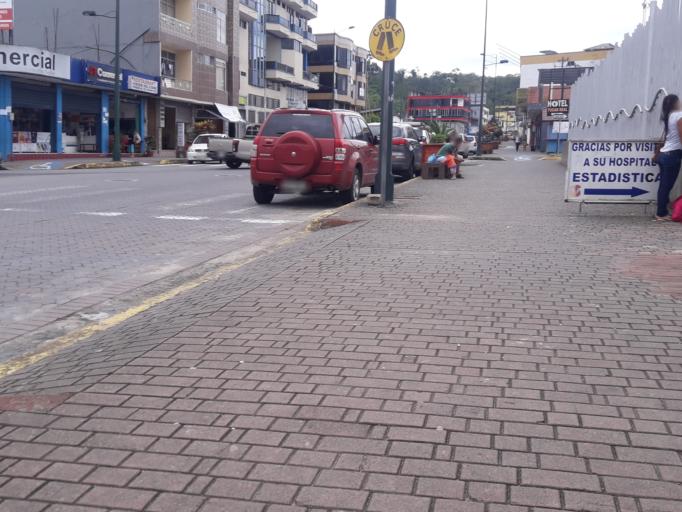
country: EC
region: Napo
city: Tena
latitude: -1.0042
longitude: -77.8109
